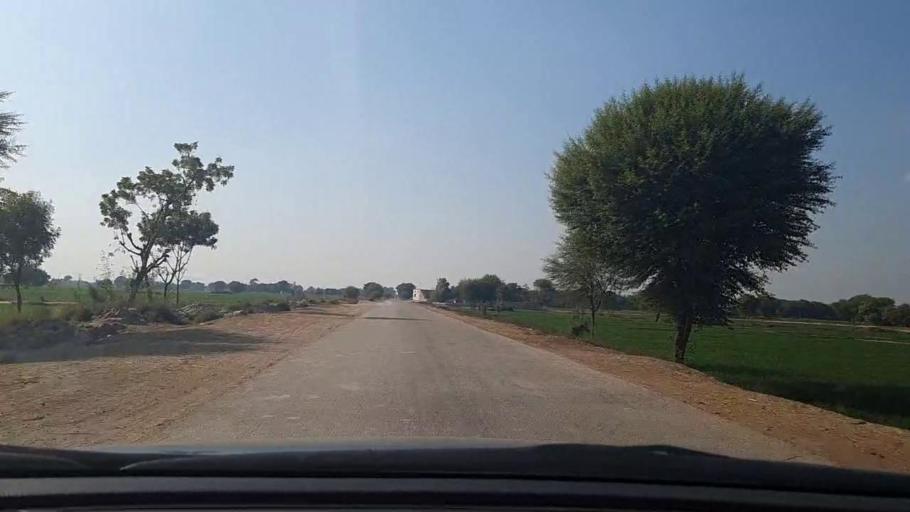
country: PK
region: Sindh
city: Daulatpur
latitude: 26.3152
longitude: 68.0665
